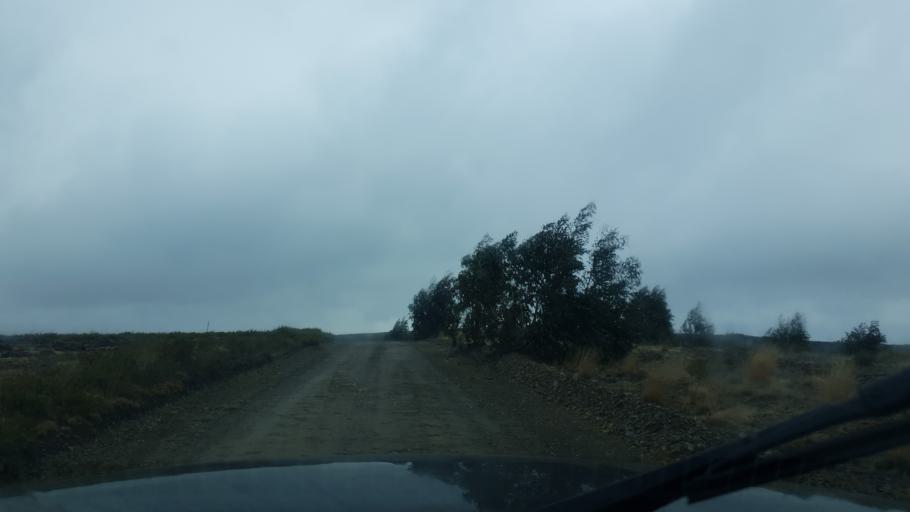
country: PT
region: Viseu
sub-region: Sao Pedro do Sul
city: Sao Pedro do Sul
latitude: 40.8531
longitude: -8.1041
